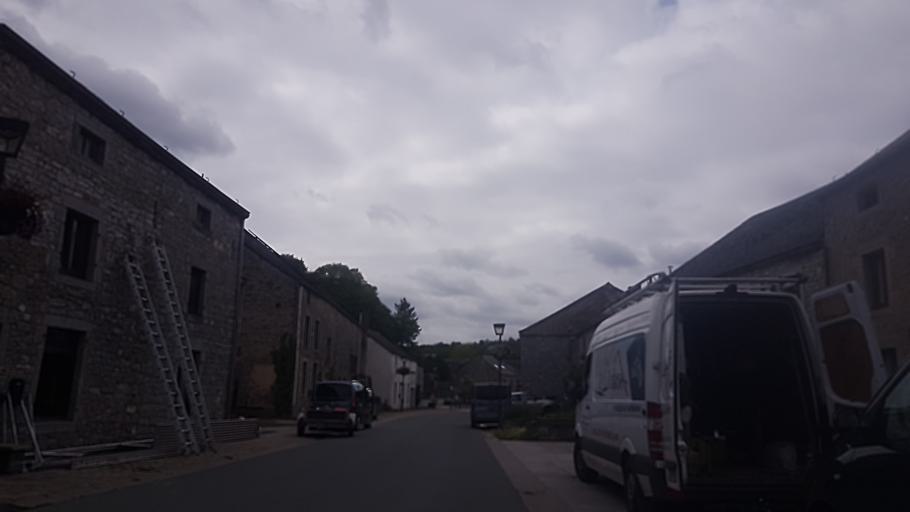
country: BE
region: Wallonia
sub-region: Province de Namur
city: Couvin
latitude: 50.0910
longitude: 4.5924
